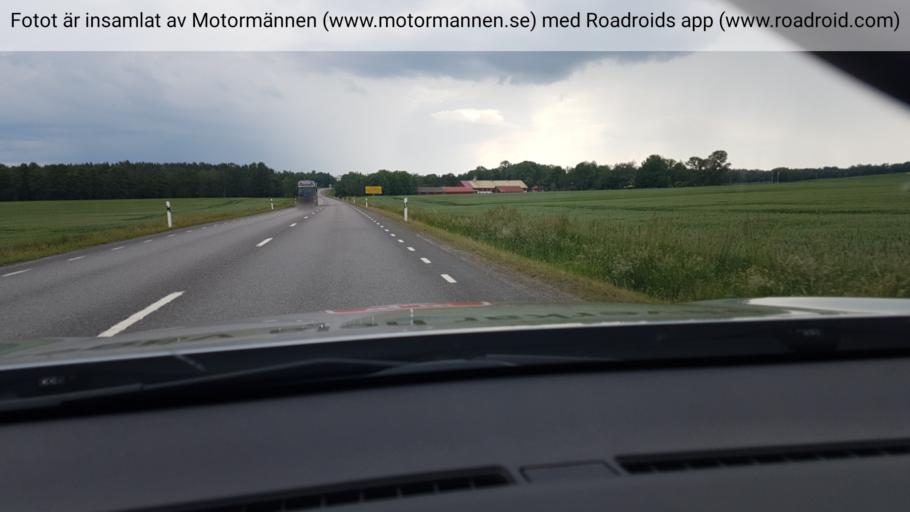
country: SE
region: Joenkoeping
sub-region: Habo Kommun
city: Habo
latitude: 57.9377
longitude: 14.0980
